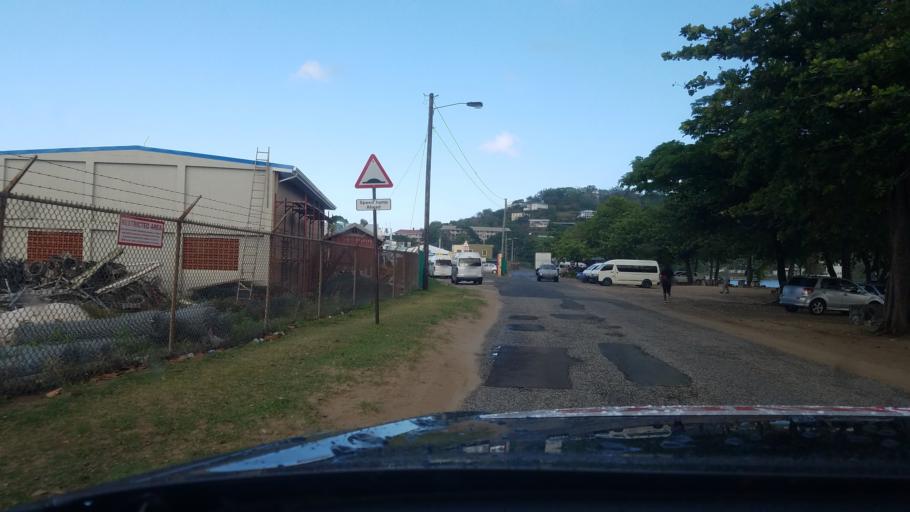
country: LC
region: Castries Quarter
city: Bisee
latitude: 14.0208
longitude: -60.9930
